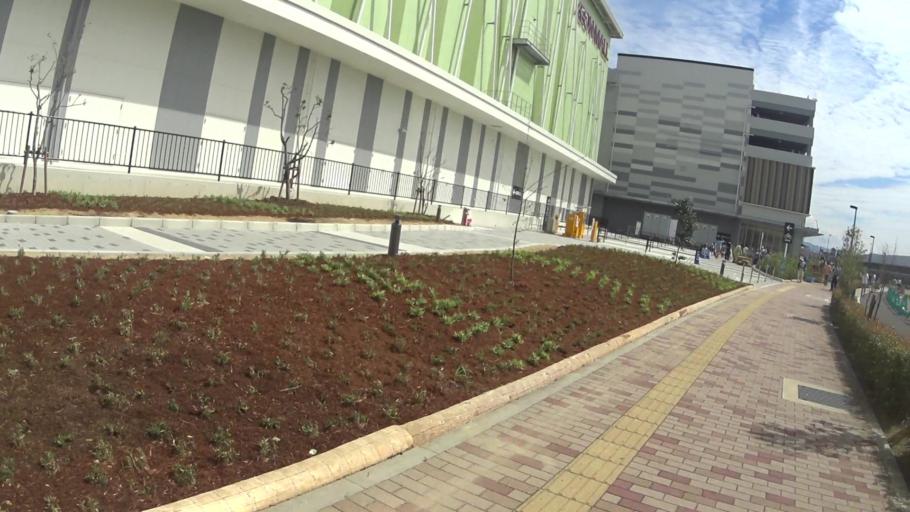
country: JP
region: Kyoto
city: Muko
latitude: 34.9616
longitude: 135.7068
